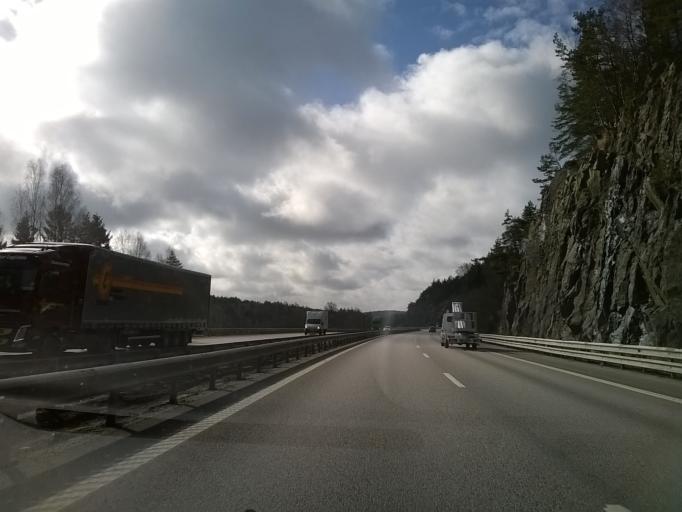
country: SE
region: Halland
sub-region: Kungsbacka Kommun
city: Fjaeras kyrkby
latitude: 57.3940
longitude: 12.1890
